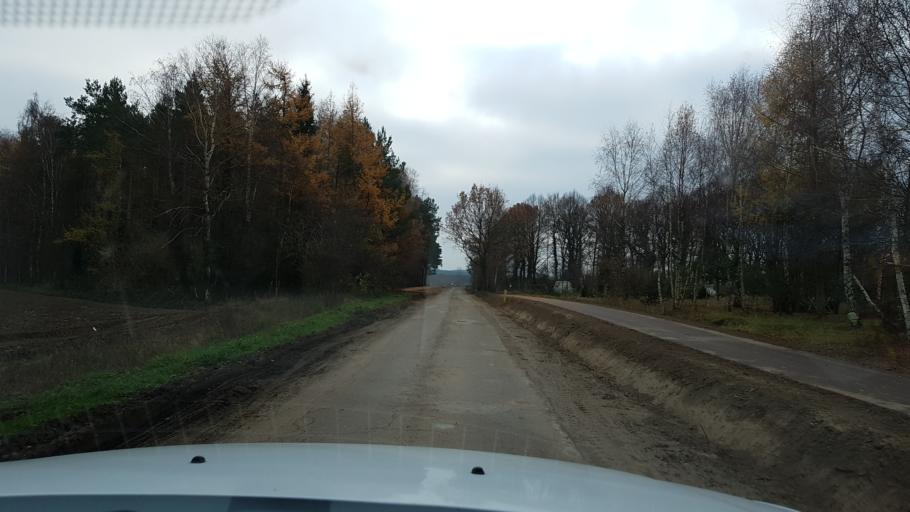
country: PL
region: West Pomeranian Voivodeship
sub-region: Powiat kolobrzeski
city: Grzybowo
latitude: 54.1138
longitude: 15.5244
